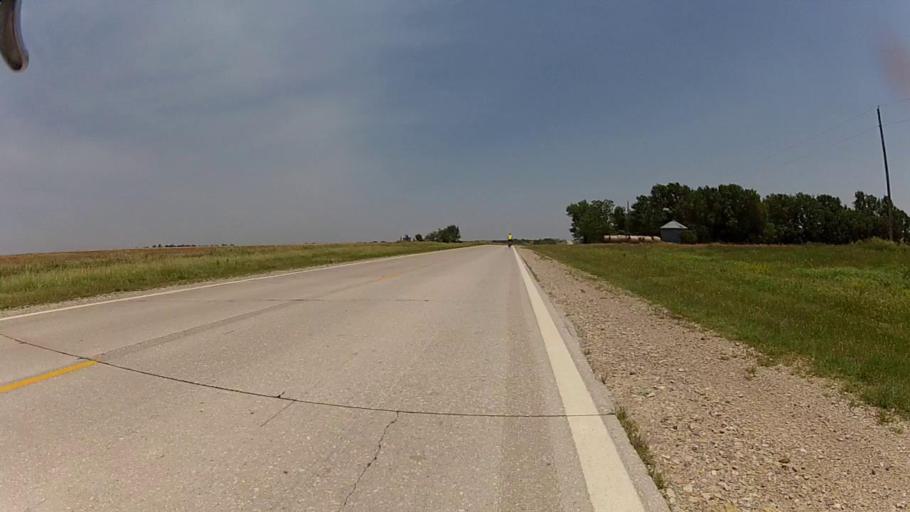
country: US
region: Kansas
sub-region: Sumner County
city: Wellington
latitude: 37.0576
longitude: -97.3568
